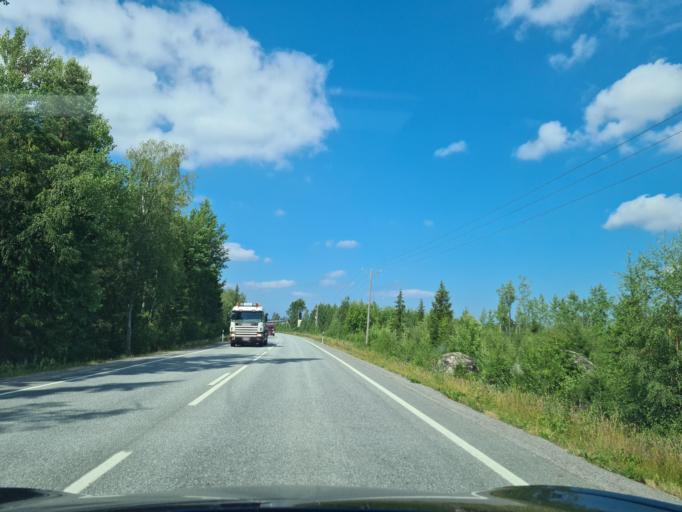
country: FI
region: Ostrobothnia
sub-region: Vaasa
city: Vaasa
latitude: 63.1648
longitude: 21.5901
